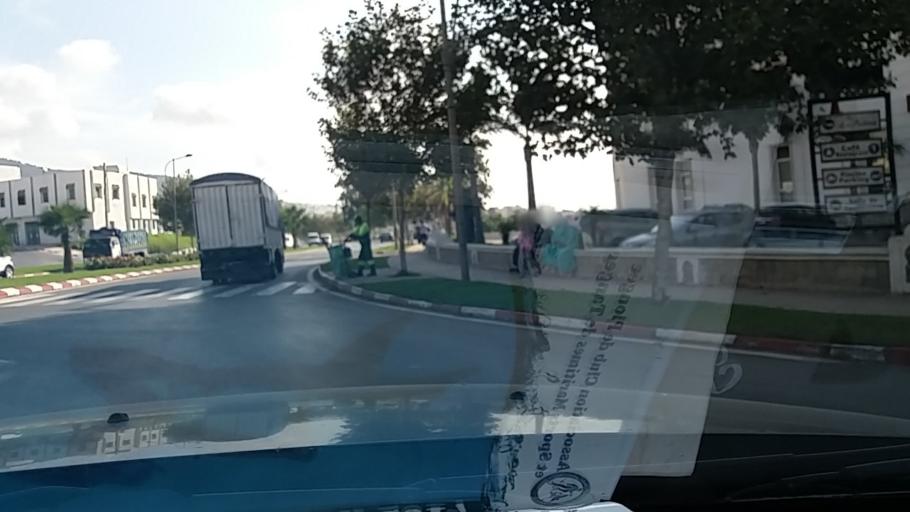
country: MA
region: Tanger-Tetouan
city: Tetouan
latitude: 35.5653
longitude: -5.4125
